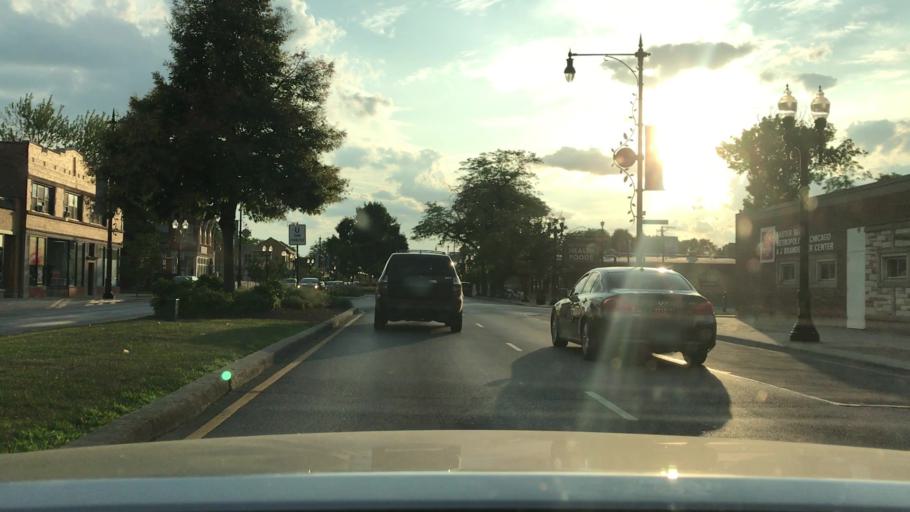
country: US
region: Illinois
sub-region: Cook County
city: Evergreen Park
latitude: 41.7211
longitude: -87.6739
